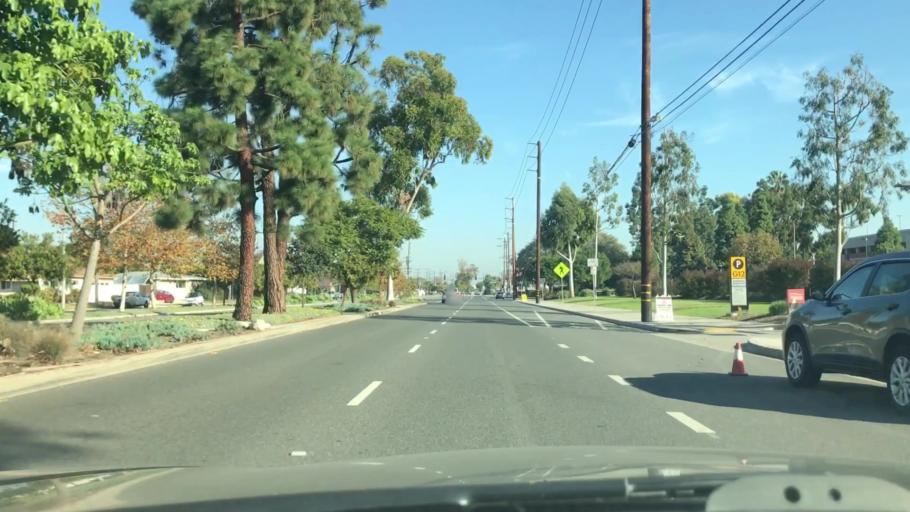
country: US
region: California
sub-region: Orange County
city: Rossmoor
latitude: 33.7886
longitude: -118.1114
